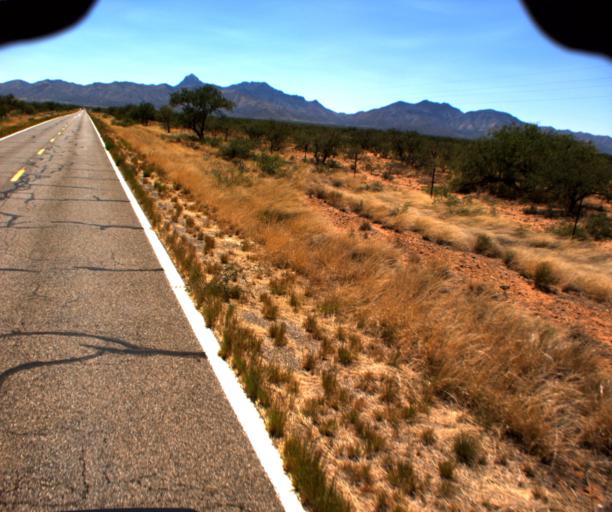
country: US
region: Arizona
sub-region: Pima County
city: Three Points
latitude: 31.8336
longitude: -111.4148
